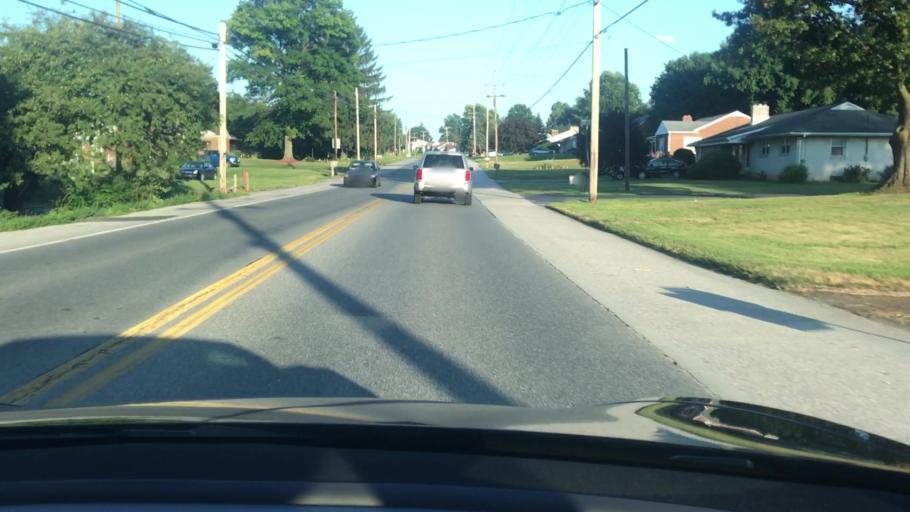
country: US
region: Pennsylvania
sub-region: York County
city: Weigelstown
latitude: 39.9871
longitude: -76.8320
